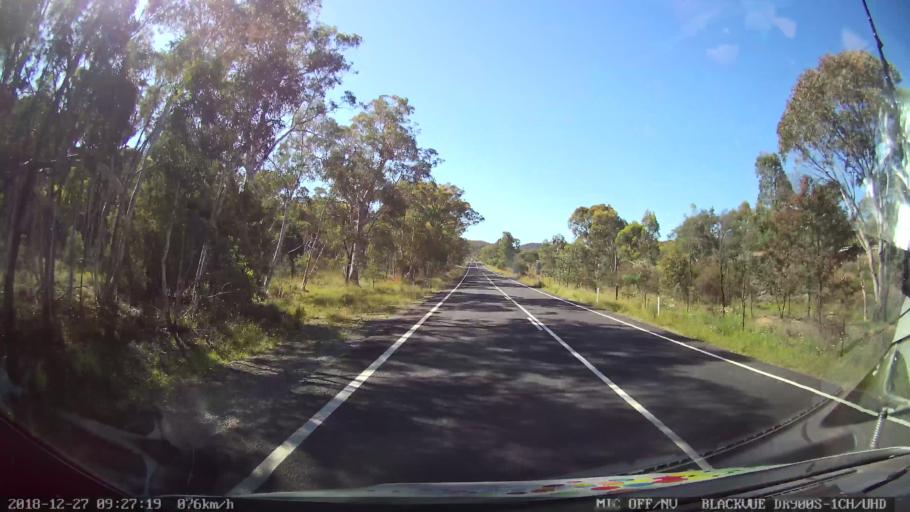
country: AU
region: New South Wales
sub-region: Lithgow
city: Portland
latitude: -33.1515
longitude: 149.9929
